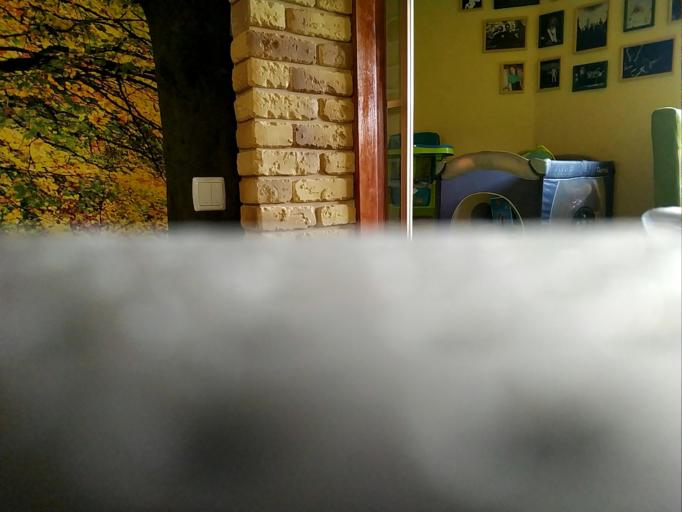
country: RU
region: Kaluga
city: Sukhinichi
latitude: 54.0491
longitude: 35.2988
